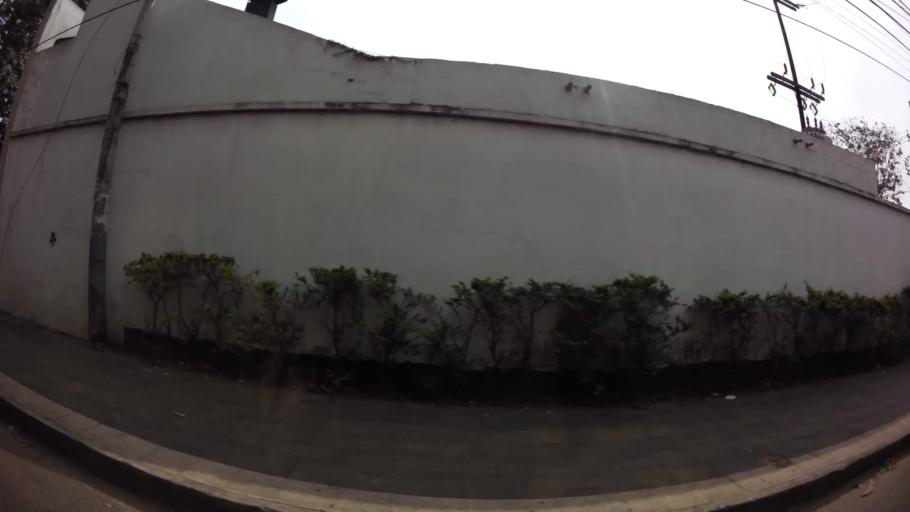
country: PY
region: Asuncion
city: Asuncion
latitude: -25.2833
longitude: -57.5714
